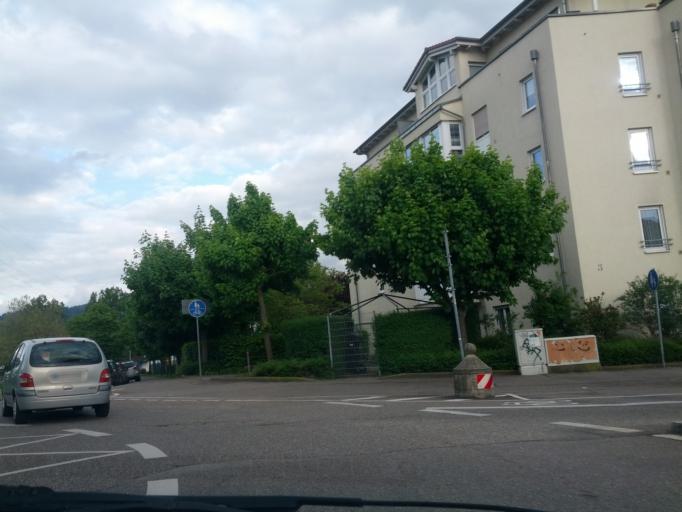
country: DE
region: Baden-Wuerttemberg
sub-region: Freiburg Region
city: Merzhausen
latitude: 47.9832
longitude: 7.8088
